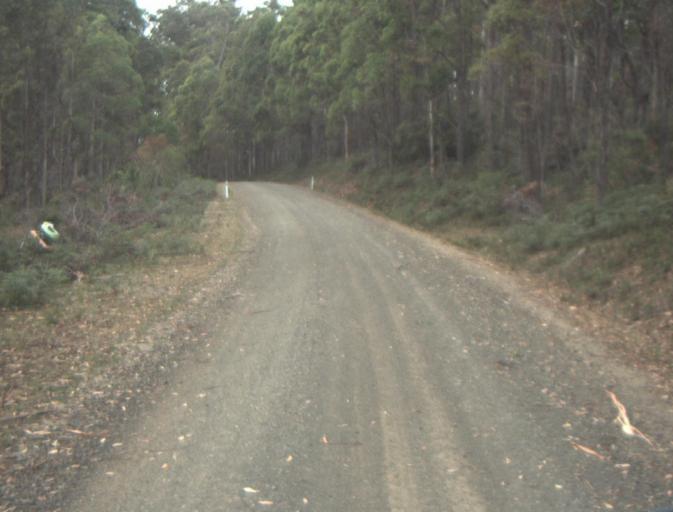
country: AU
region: Tasmania
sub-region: Dorset
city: Scottsdale
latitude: -41.4108
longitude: 147.5169
